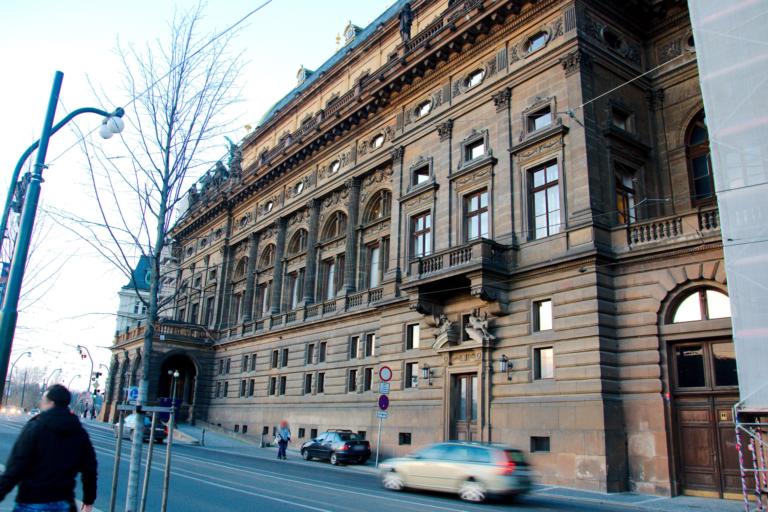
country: CZ
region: Praha
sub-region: Praha 1
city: Stare Mesto
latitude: 50.0802
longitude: 14.4135
